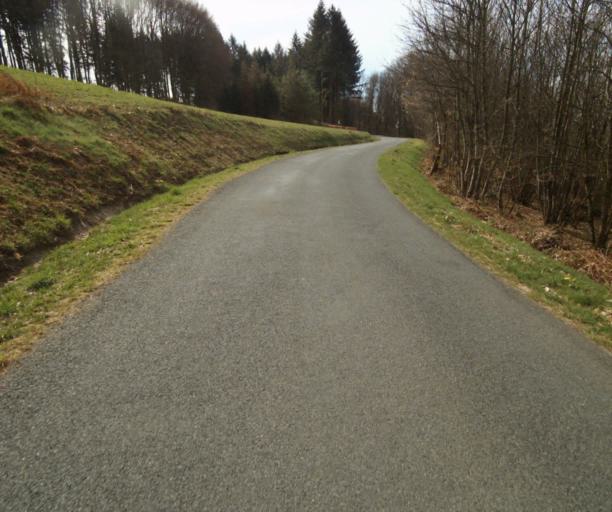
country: FR
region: Limousin
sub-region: Departement de la Correze
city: Correze
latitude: 45.3744
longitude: 1.9021
